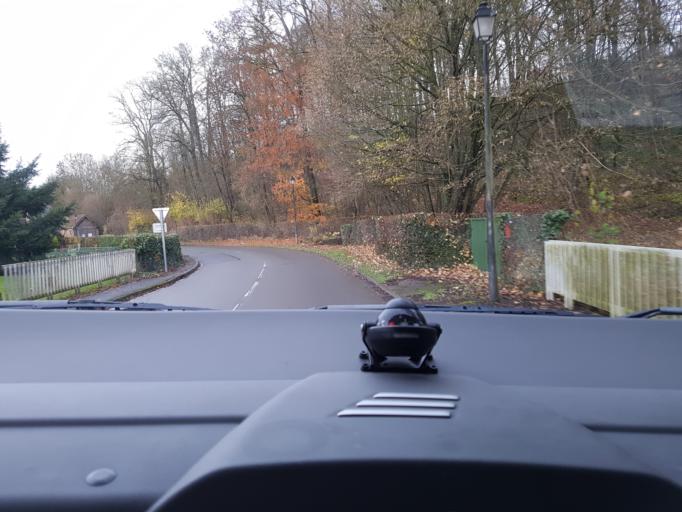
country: FR
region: Picardie
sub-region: Departement de l'Oise
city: Songeons
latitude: 49.5512
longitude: 1.8553
